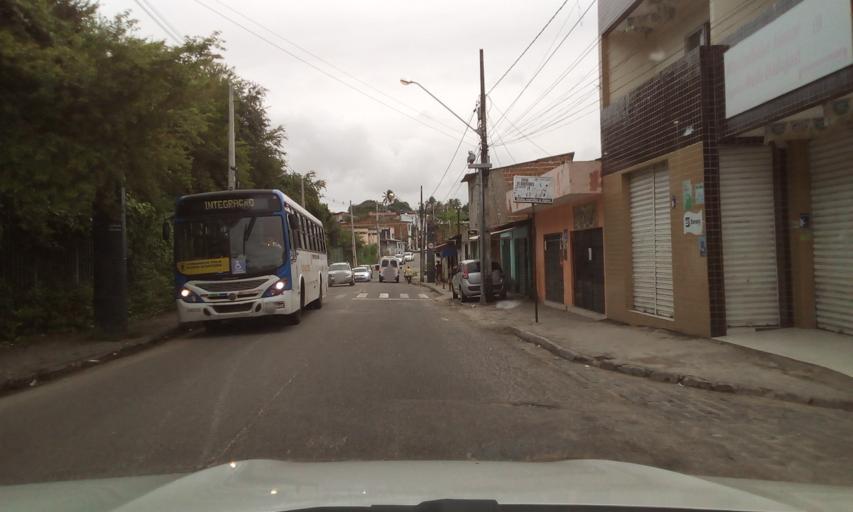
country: BR
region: Paraiba
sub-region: Joao Pessoa
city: Joao Pessoa
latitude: -7.1069
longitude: -34.8721
